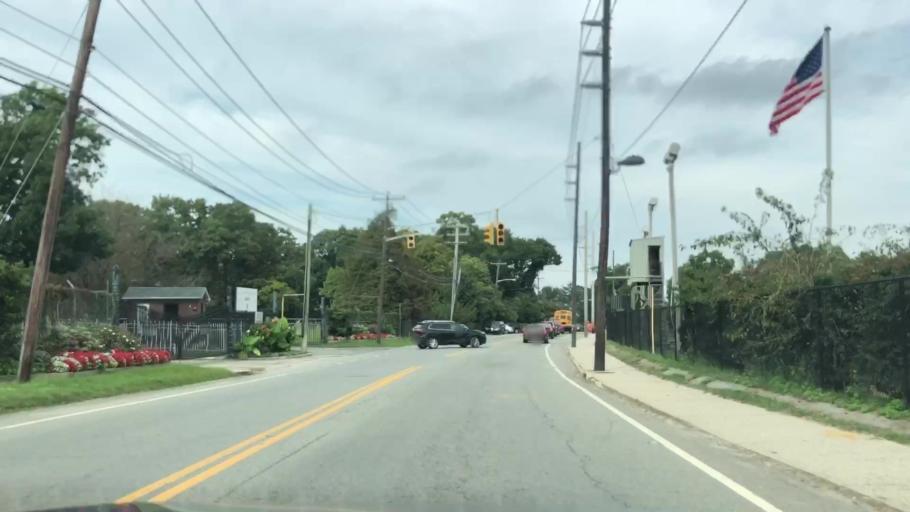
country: US
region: New York
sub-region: Nassau County
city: South Floral Park
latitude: 40.7145
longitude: -73.7080
